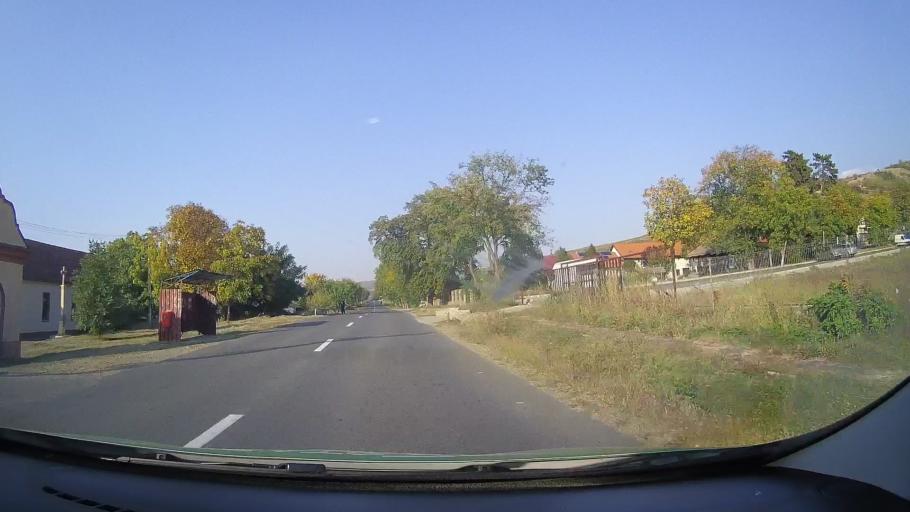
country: RO
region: Arad
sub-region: Comuna Paulis
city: Paulis
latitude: 46.1238
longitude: 21.5985
